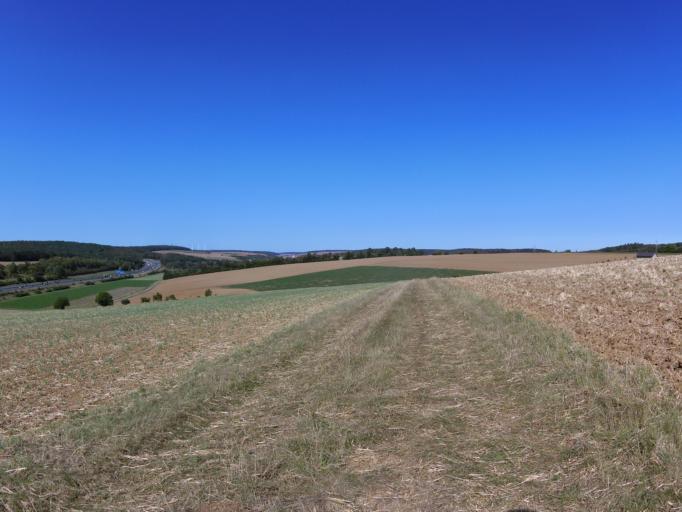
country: DE
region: Bavaria
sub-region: Regierungsbezirk Unterfranken
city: Waldbrunn
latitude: 49.7575
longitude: 9.7886
